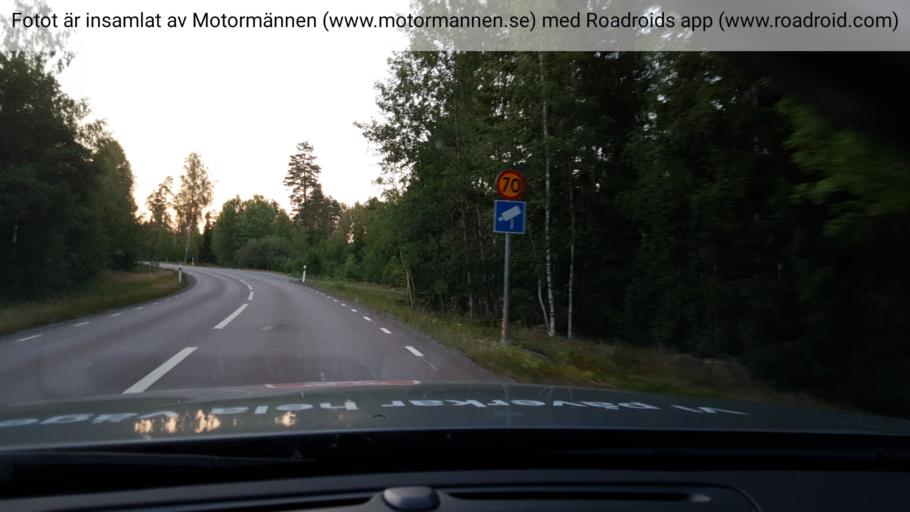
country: SE
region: Uppsala
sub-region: Heby Kommun
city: OEstervala
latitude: 60.0222
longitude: 17.2823
